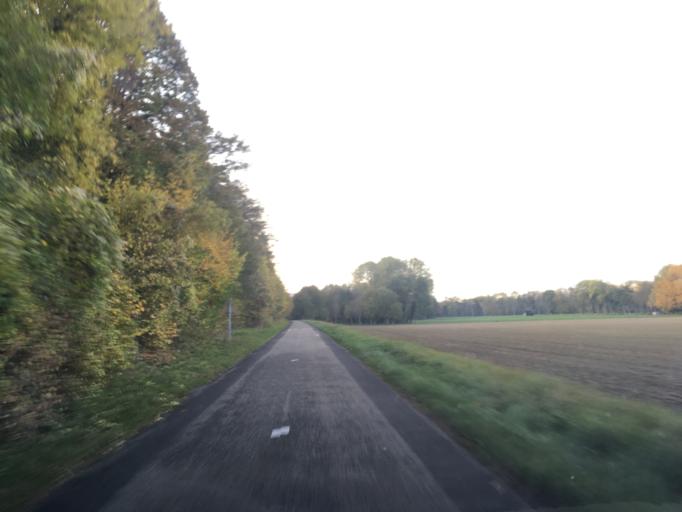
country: FR
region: Haute-Normandie
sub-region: Departement de l'Eure
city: Heudreville-sur-Eure
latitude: 49.1030
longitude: 1.2297
